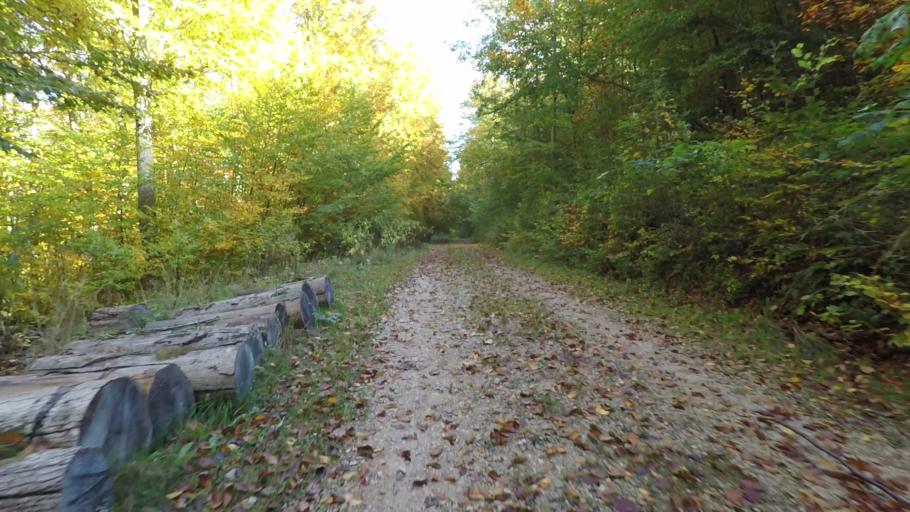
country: DE
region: Baden-Wuerttemberg
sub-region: Tuebingen Region
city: Pfullingen
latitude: 48.4282
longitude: 9.2262
